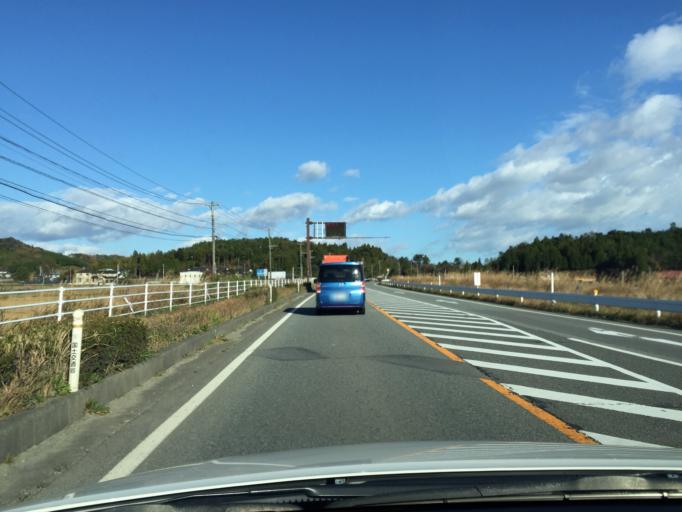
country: JP
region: Fukushima
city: Namie
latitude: 37.3024
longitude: 140.9940
